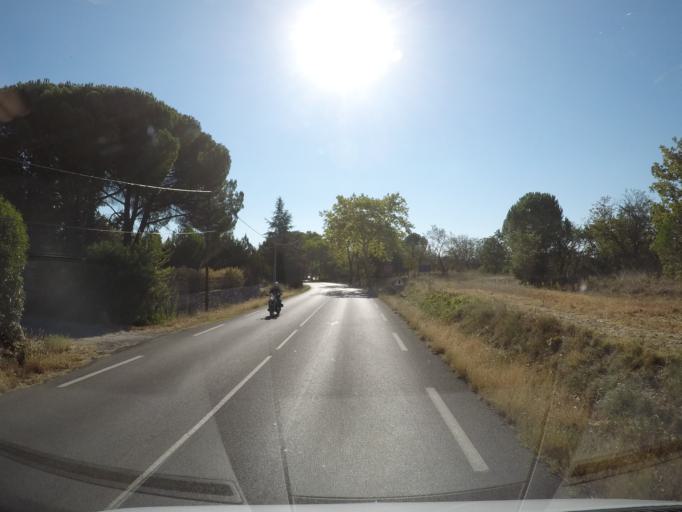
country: FR
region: Languedoc-Roussillon
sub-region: Departement du Gard
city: Boisset-et-Gaujac
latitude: 44.0315
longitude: 4.0115
